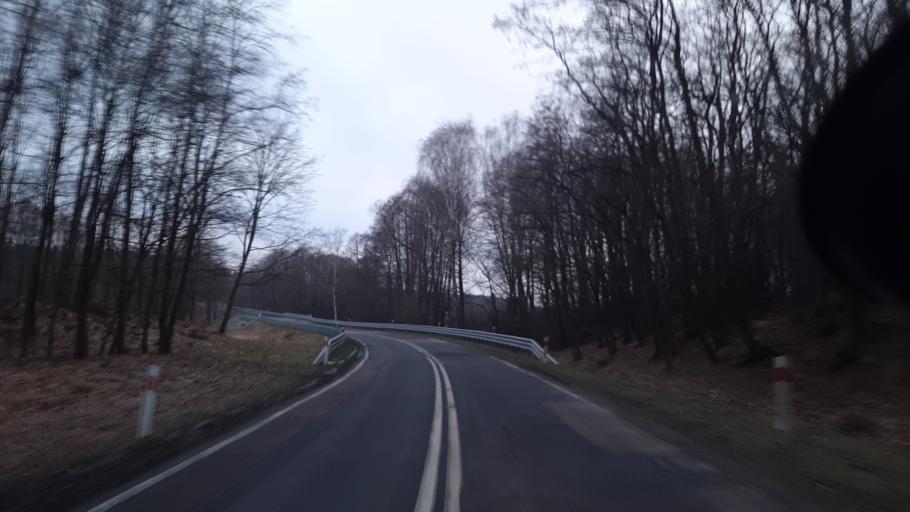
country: PL
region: Lublin Voivodeship
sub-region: Powiat parczewski
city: Debowa Kloda
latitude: 51.6395
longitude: 23.0244
